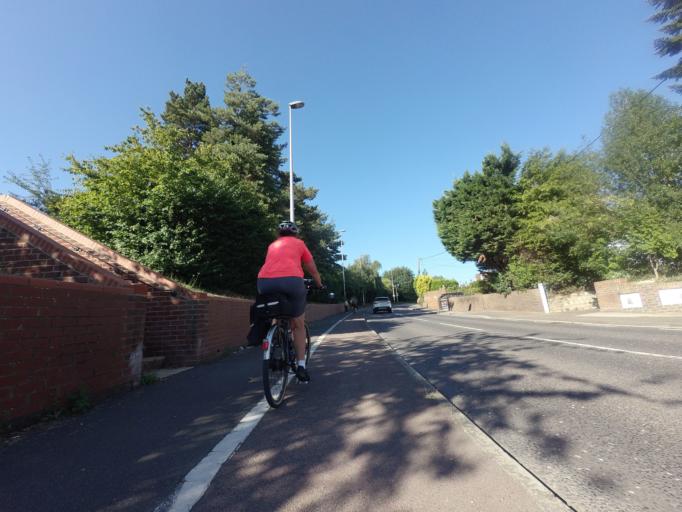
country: GB
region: England
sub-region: Kent
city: Strood
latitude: 51.4083
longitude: 0.4939
